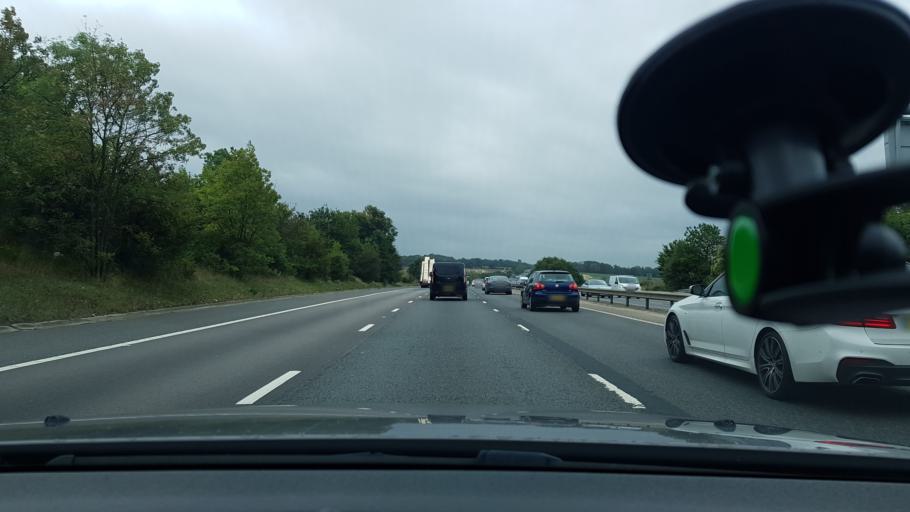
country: GB
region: England
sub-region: Hertfordshire
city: Sawbridgeworth
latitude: 51.7994
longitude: 0.1755
